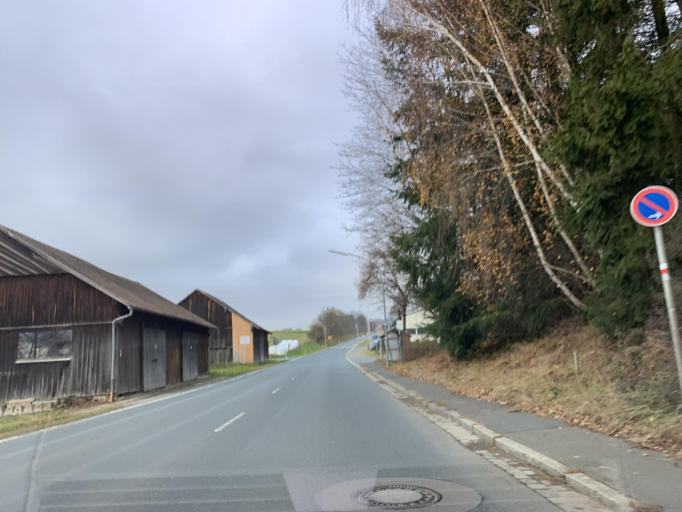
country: DE
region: Bavaria
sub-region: Upper Palatinate
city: Roetz
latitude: 49.3429
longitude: 12.5210
